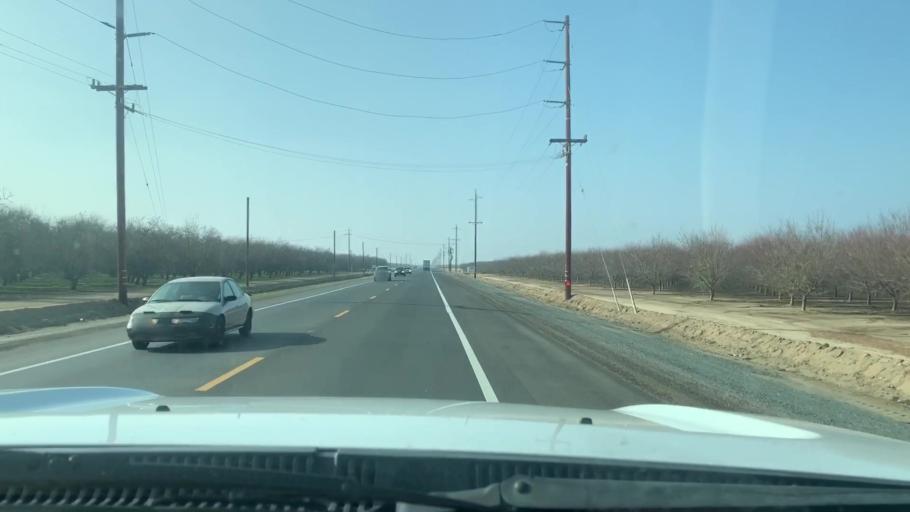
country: US
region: California
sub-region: Kern County
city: McFarland
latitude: 35.6019
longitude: -119.2567
